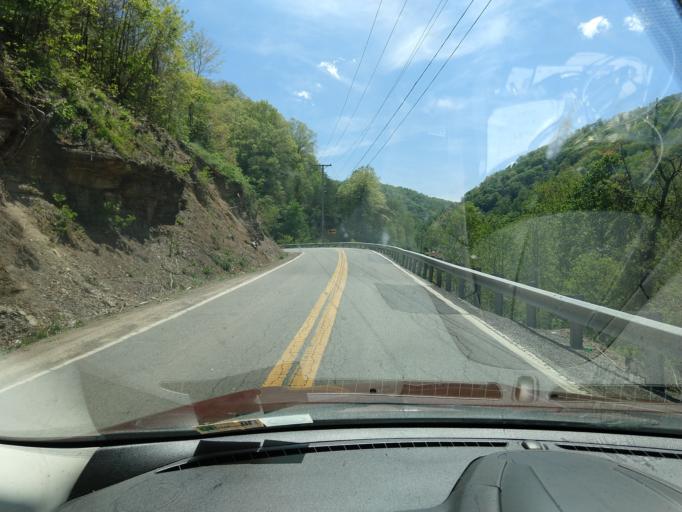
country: US
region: West Virginia
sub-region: McDowell County
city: Welch
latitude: 37.3093
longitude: -81.6930
